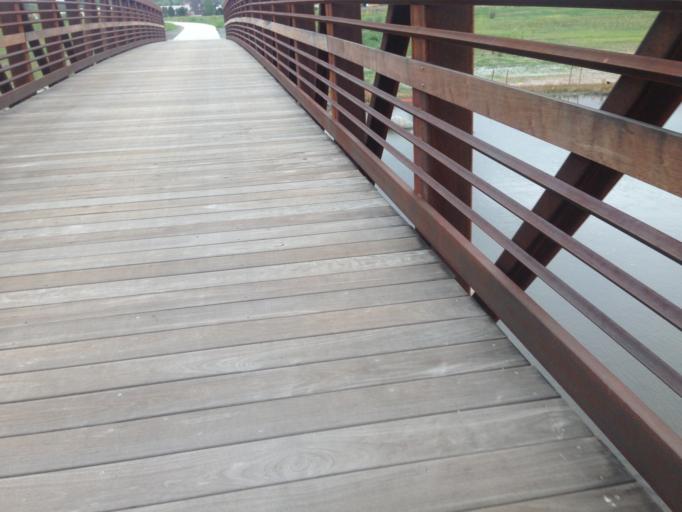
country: US
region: Colorado
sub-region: Boulder County
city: Longmont
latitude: 40.1546
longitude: -105.0960
